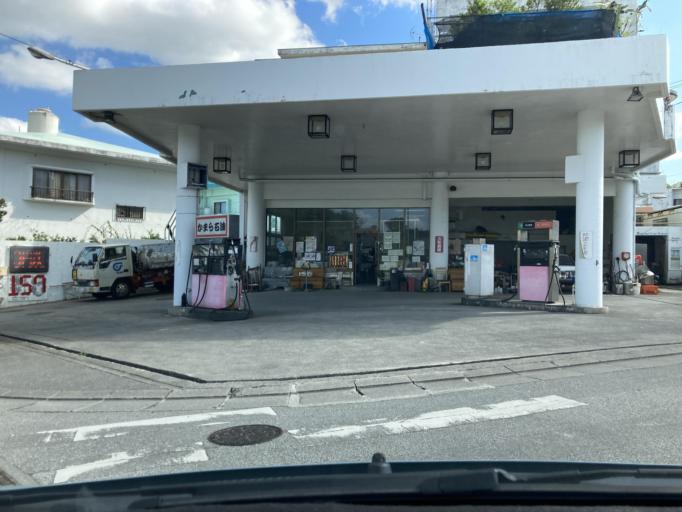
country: JP
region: Okinawa
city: Okinawa
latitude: 26.3435
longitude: 127.8030
